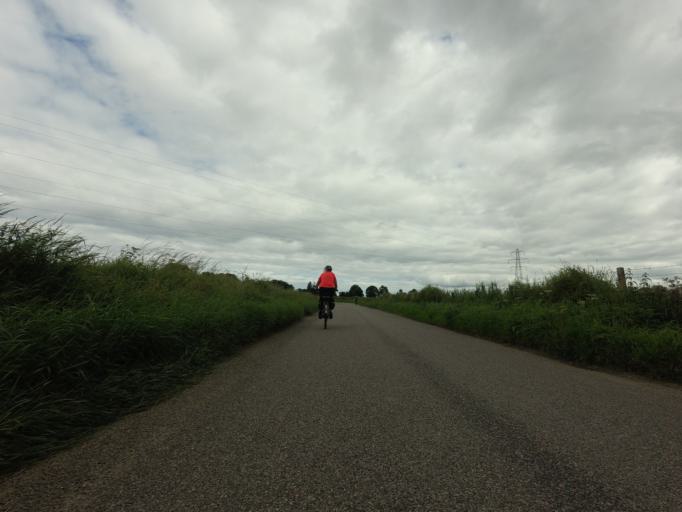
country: GB
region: Scotland
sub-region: Moray
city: Forres
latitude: 57.6149
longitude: -3.6540
